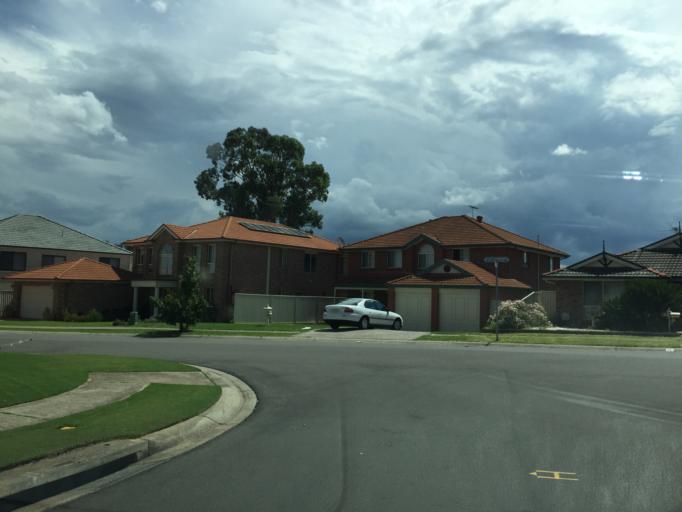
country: AU
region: New South Wales
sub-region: Blacktown
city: Doonside
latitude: -33.7822
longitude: 150.8802
